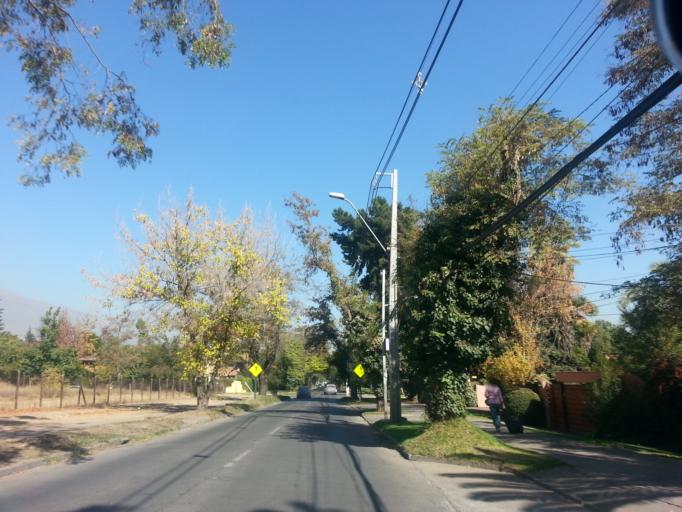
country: CL
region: Santiago Metropolitan
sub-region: Provincia de Santiago
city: Villa Presidente Frei, Nunoa, Santiago, Chile
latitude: -33.4359
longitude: -70.5429
